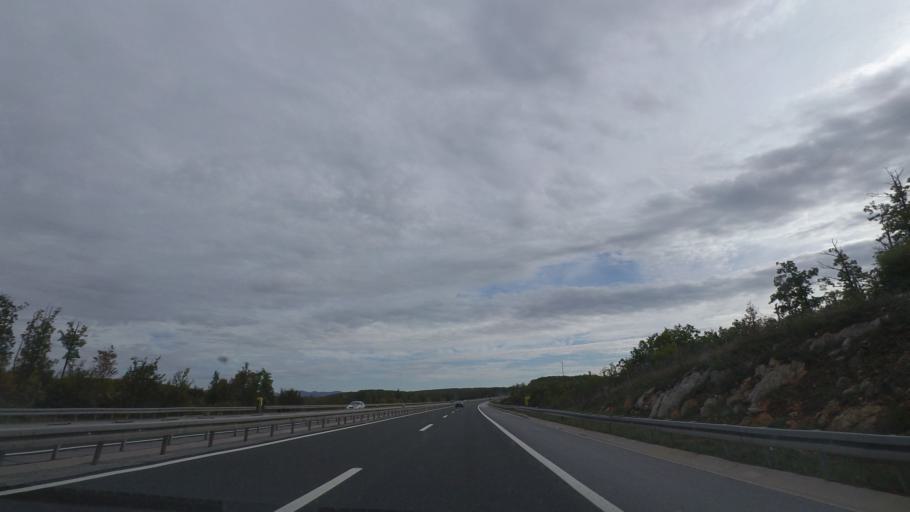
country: HR
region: Licko-Senjska
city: Gospic
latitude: 44.7300
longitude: 15.3837
